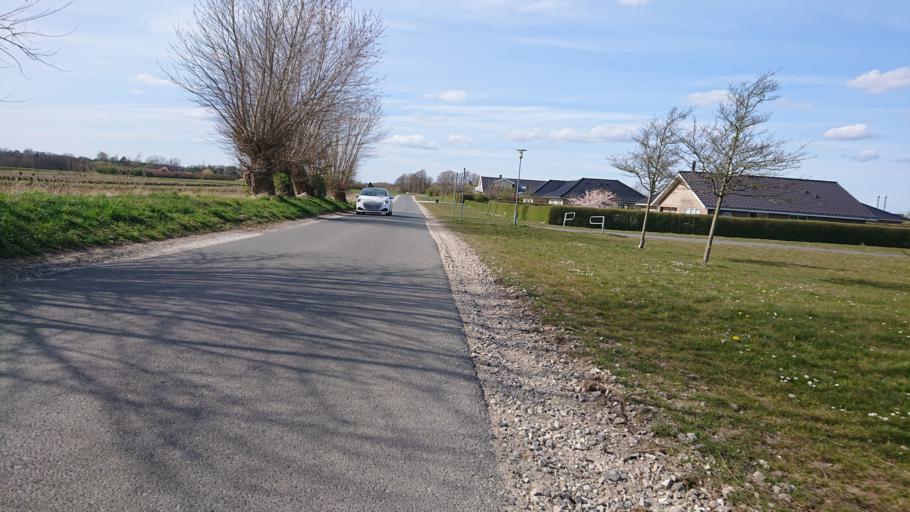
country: DK
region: South Denmark
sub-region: Nyborg Kommune
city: Nyborg
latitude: 55.3080
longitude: 10.7481
